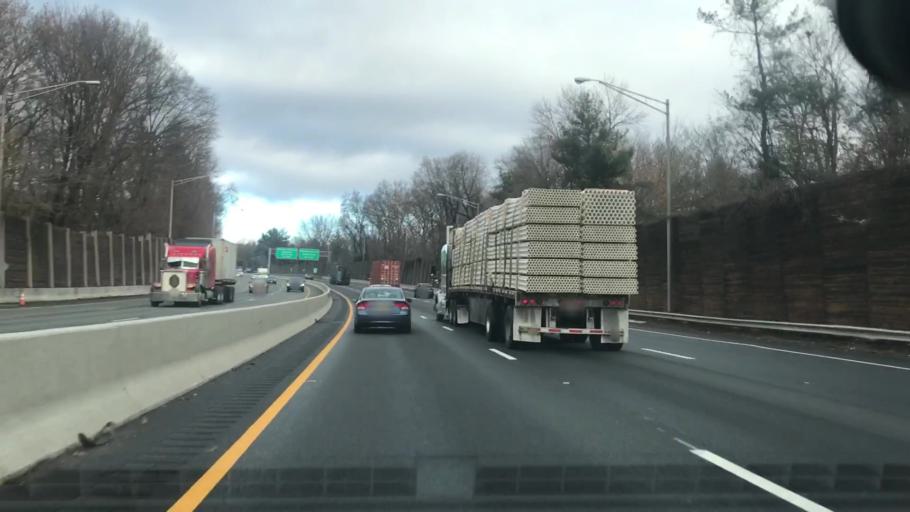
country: US
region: New Jersey
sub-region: Bergen County
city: Ho-Ho-Kus
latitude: 41.0055
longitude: -74.1025
